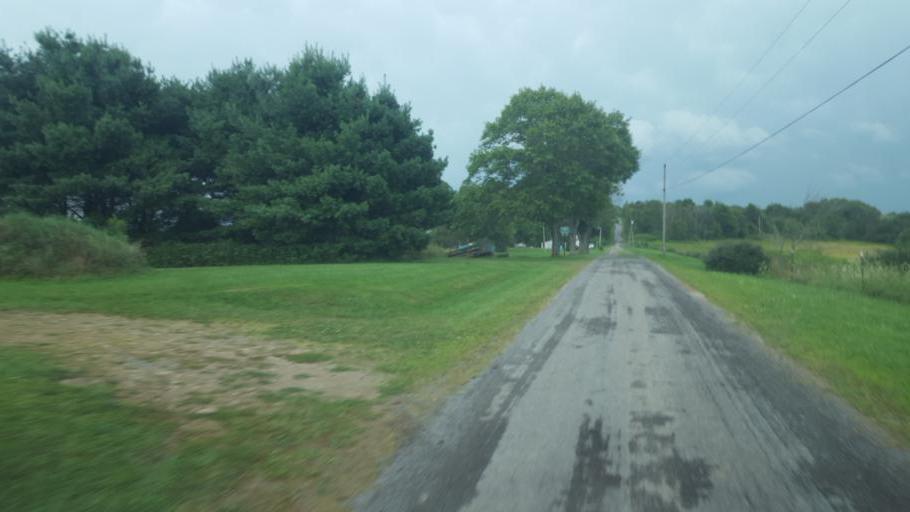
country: US
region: Pennsylvania
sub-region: Clarion County
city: Knox
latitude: 41.1471
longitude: -79.5145
